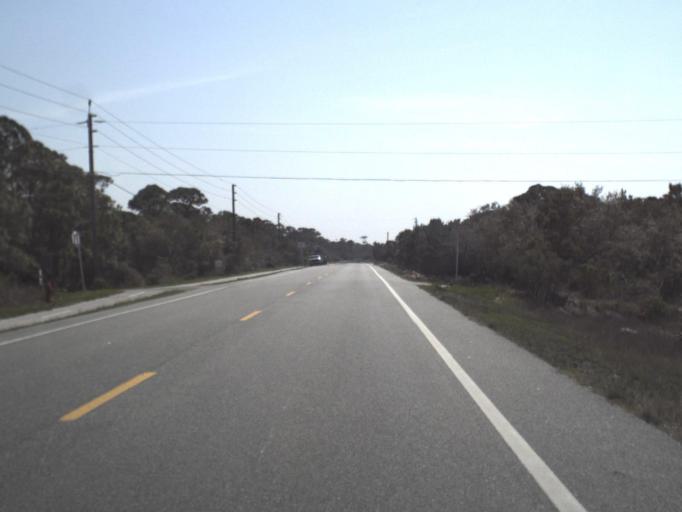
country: US
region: Florida
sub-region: Gulf County
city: Port Saint Joe
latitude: 29.7168
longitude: -85.3842
